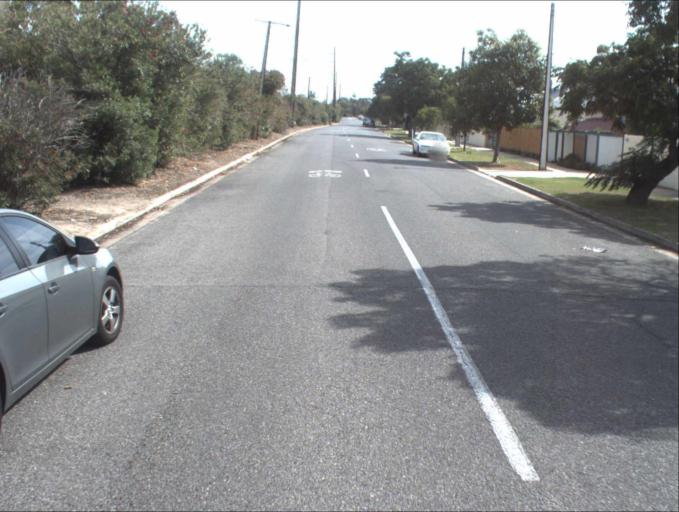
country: AU
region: South Australia
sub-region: Port Adelaide Enfield
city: Birkenhead
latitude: -34.8298
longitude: 138.4917
